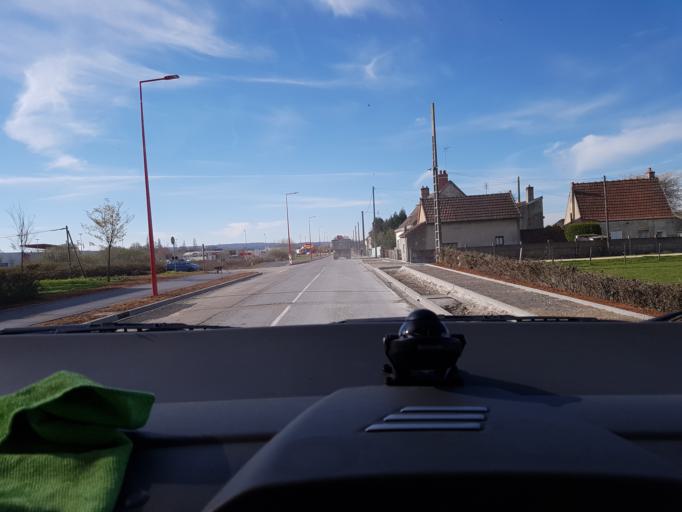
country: FR
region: Bourgogne
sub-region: Departement de Saone-et-Loire
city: Gueugnon
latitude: 46.5932
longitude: 4.0659
